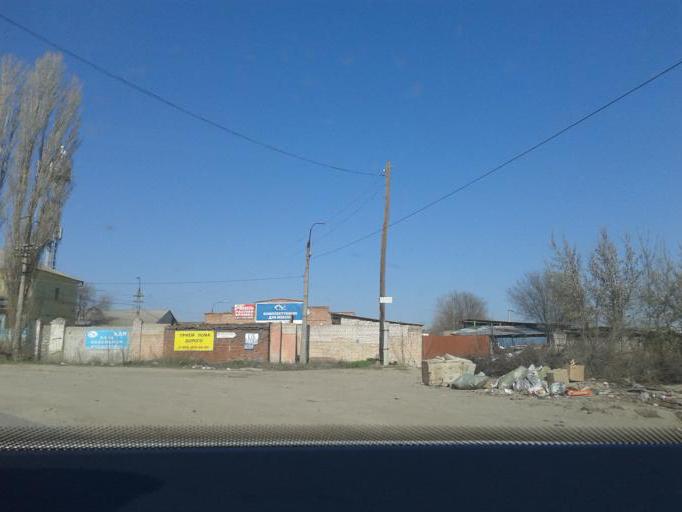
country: RU
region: Volgograd
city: Volgograd
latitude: 48.6823
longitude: 44.4583
